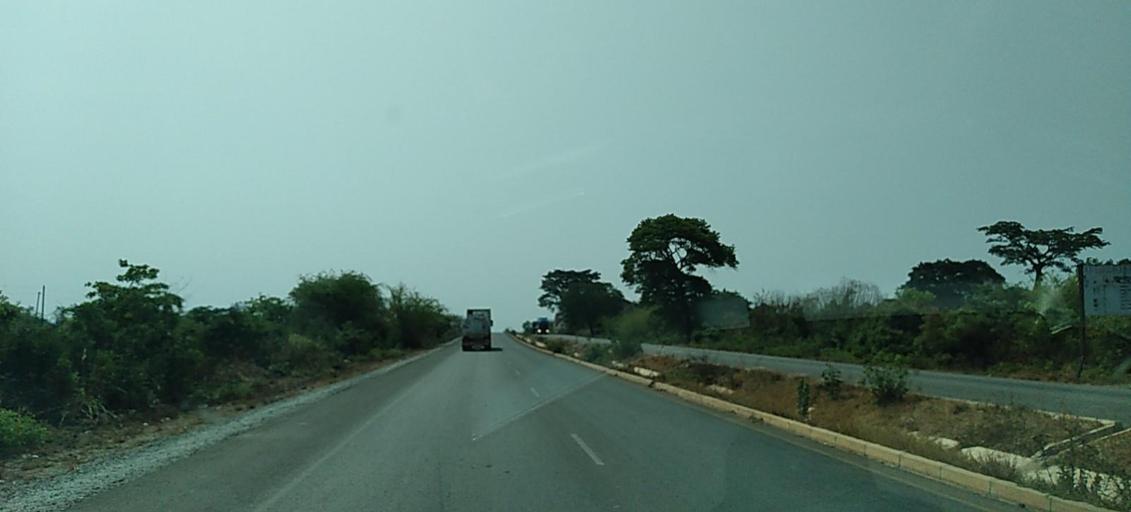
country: ZM
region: Copperbelt
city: Chingola
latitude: -12.5787
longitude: 27.9238
